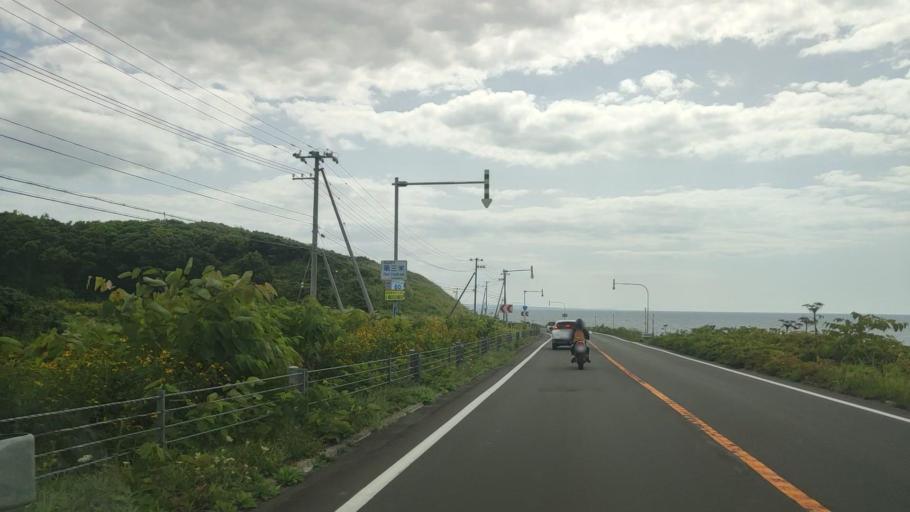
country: JP
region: Hokkaido
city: Rumoi
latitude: 44.5102
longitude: 141.7653
